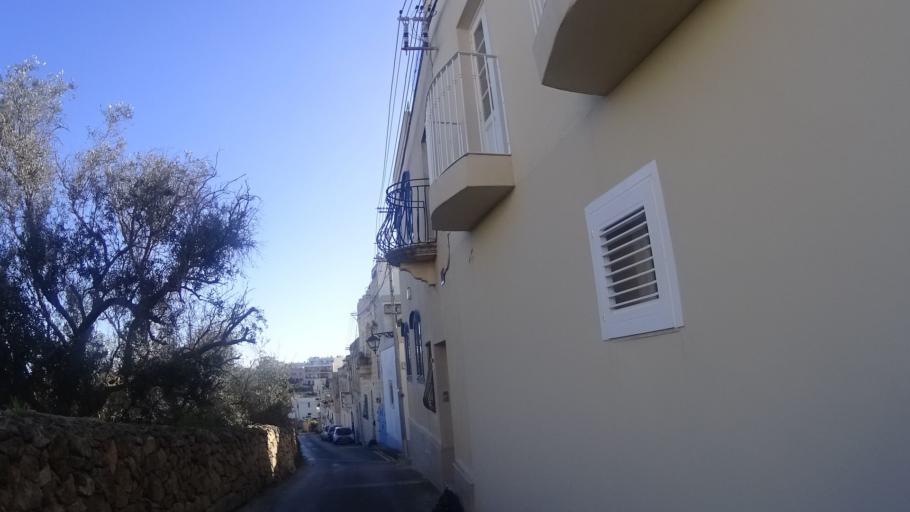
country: MT
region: Hal Gharghur
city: Hal Gharghur
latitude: 35.9254
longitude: 14.4531
